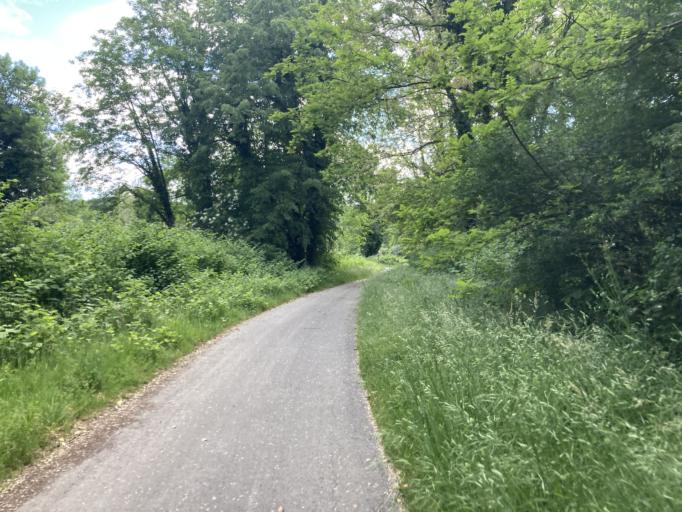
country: FR
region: Aquitaine
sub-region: Departement des Pyrenees-Atlantiques
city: Arbus
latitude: 43.3473
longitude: -0.5114
